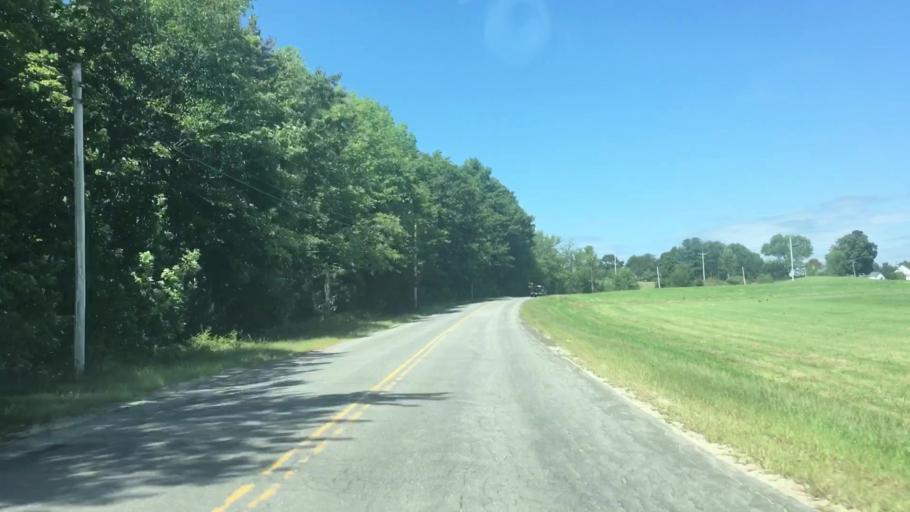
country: US
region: Maine
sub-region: Androscoggin County
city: Lisbon
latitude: 44.0716
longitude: -70.1149
